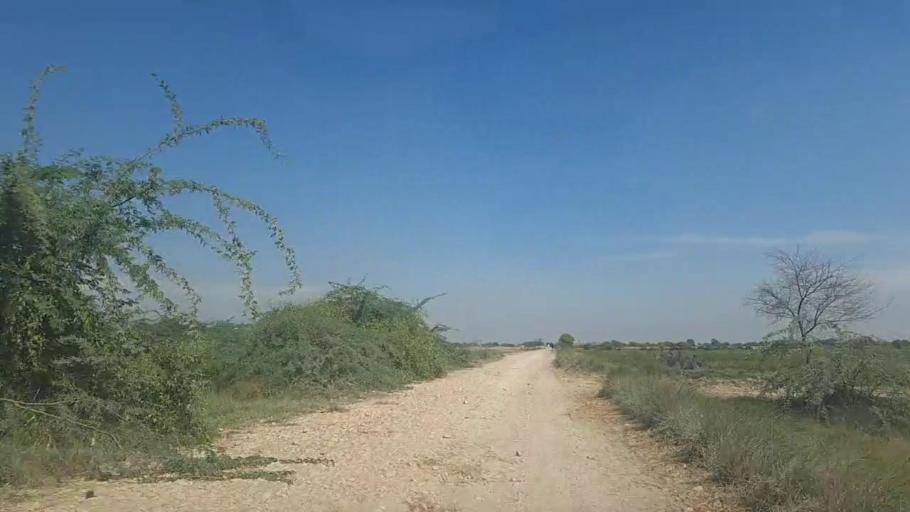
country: PK
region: Sindh
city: Mirpur Batoro
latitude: 24.7042
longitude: 68.2398
